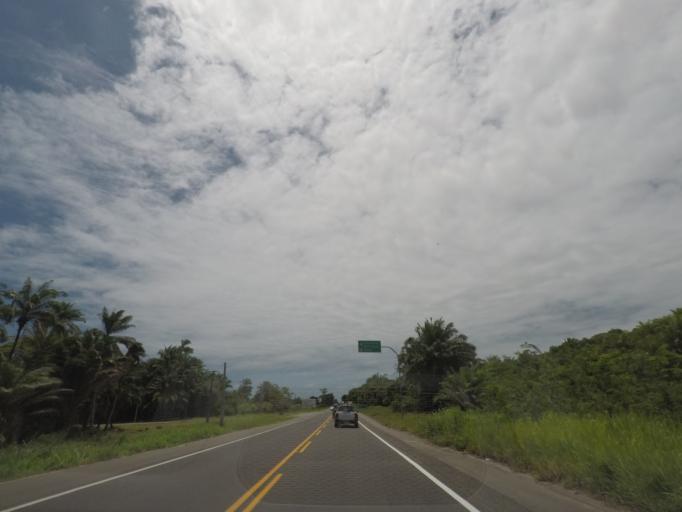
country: BR
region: Bahia
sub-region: Itaparica
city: Itaparica
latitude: -12.9844
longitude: -38.6322
